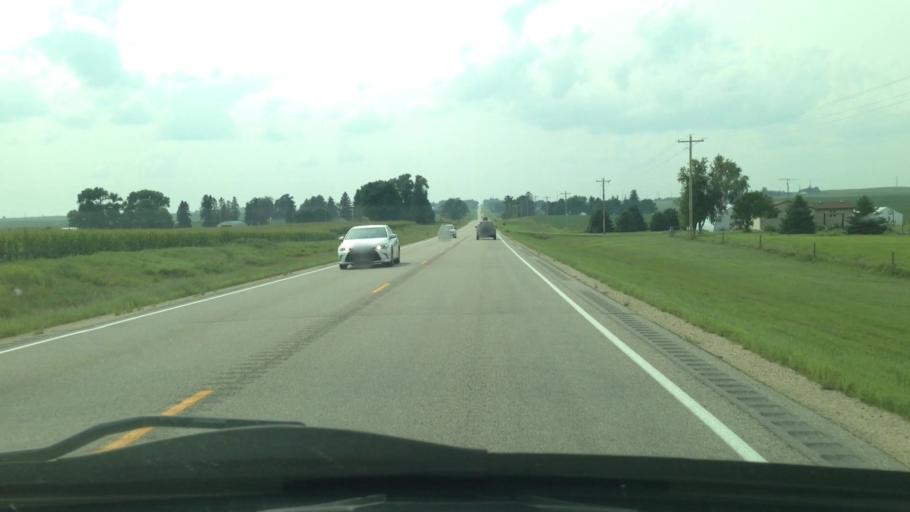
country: US
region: Minnesota
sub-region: Wabasha County
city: Elgin
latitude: 44.1657
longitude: -92.3491
